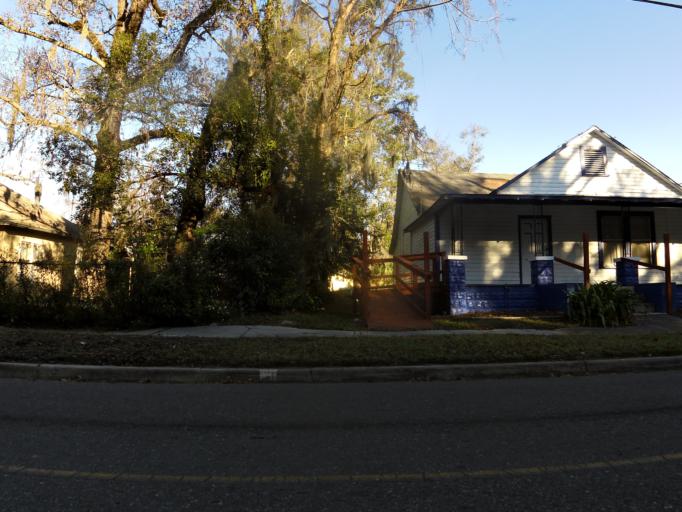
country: US
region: Florida
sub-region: Duval County
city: Jacksonville
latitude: 30.3258
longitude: -81.6968
